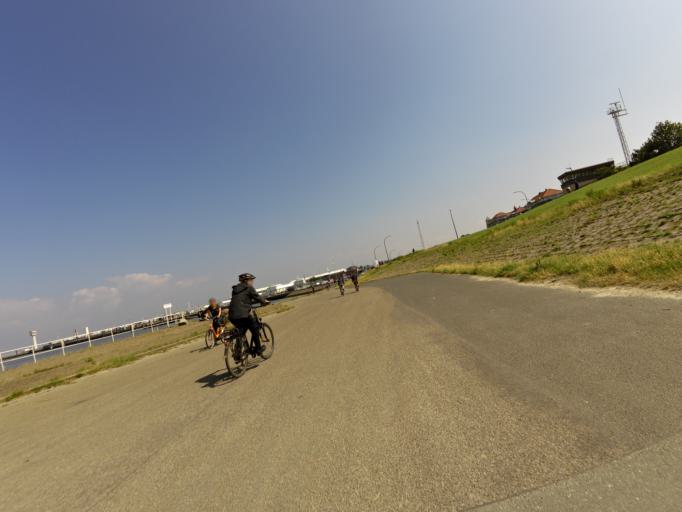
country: DE
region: Lower Saxony
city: Cuxhaven
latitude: 53.8762
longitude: 8.6970
